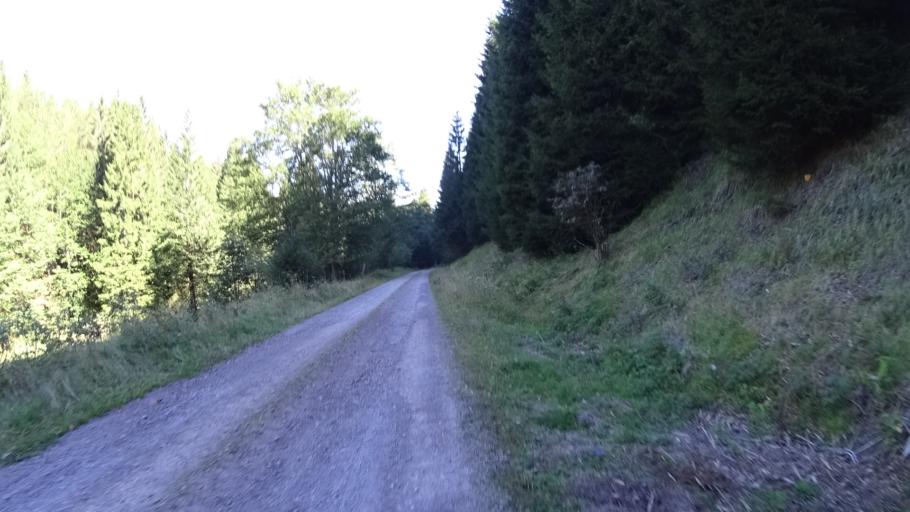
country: DE
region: Thuringia
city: Neustadt am Rennsteig
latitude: 50.6172
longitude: 10.9084
